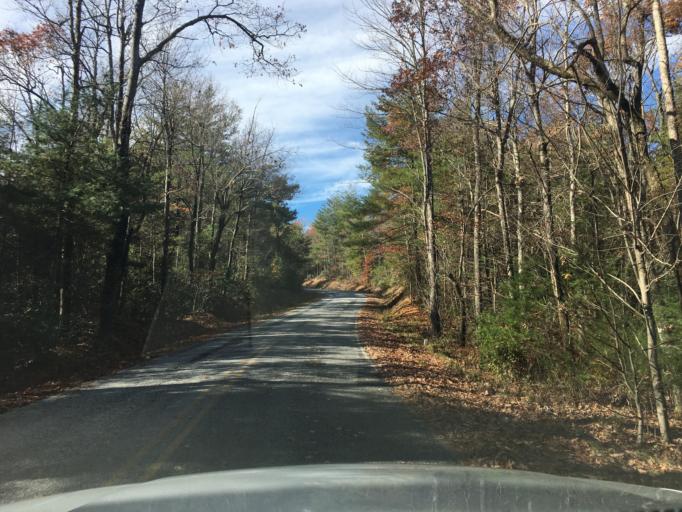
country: US
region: North Carolina
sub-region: Henderson County
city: Valley Hill
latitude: 35.2332
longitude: -82.5147
